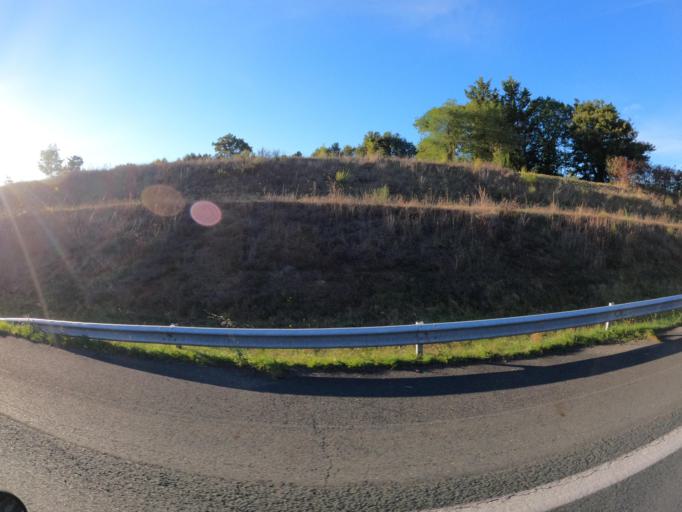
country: FR
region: Pays de la Loire
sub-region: Departement de Maine-et-Loire
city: La Tessoualle
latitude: 47.0286
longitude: -0.8624
